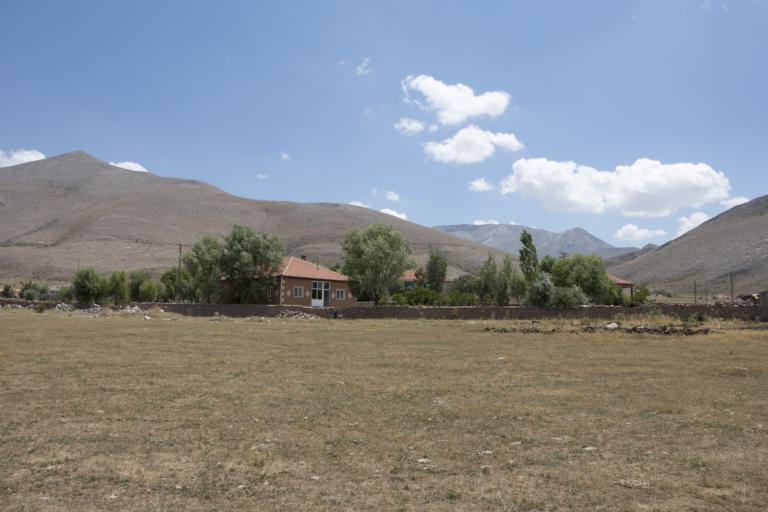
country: TR
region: Kayseri
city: Toklar
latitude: 38.4244
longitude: 36.0966
